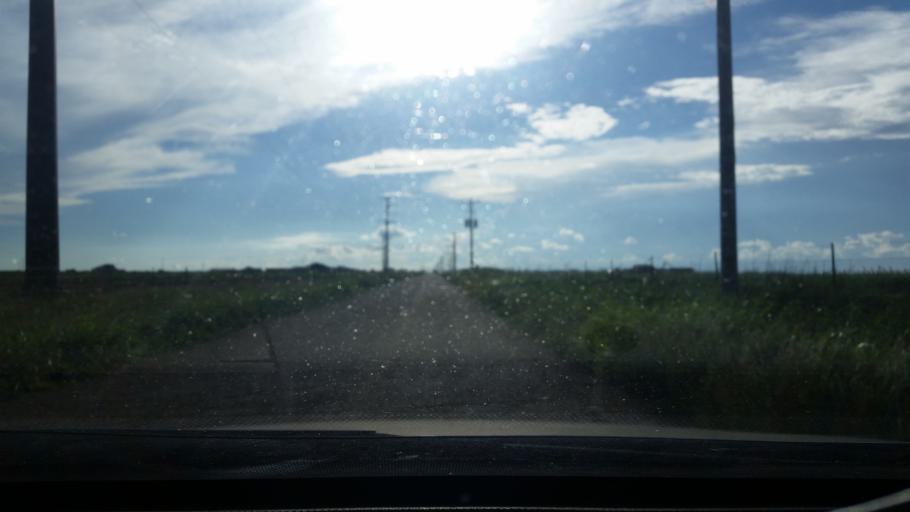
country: US
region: New Mexico
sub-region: Curry County
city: Clovis
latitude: 34.5066
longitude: -103.1903
